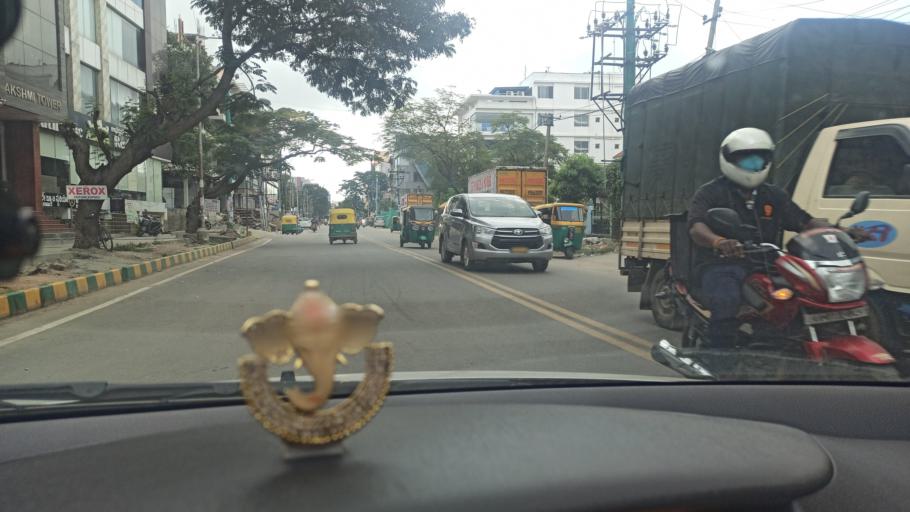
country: IN
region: Karnataka
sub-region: Bangalore Urban
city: Bangalore
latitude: 12.9102
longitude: 77.6324
